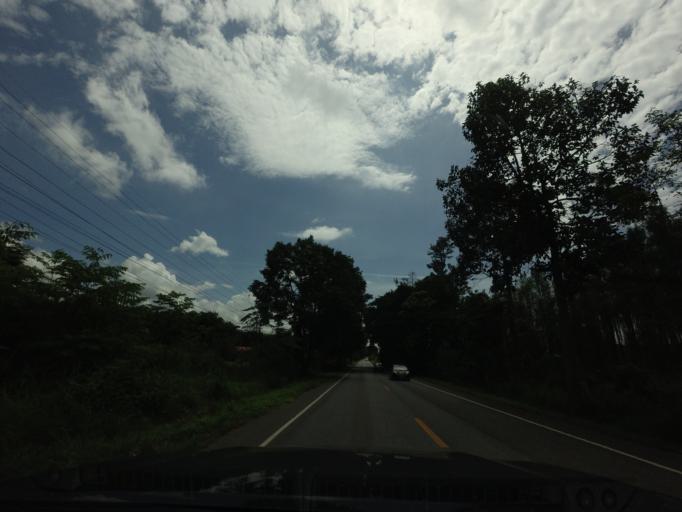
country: TH
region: Nong Khai
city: Pho Tak
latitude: 17.8043
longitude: 102.3427
